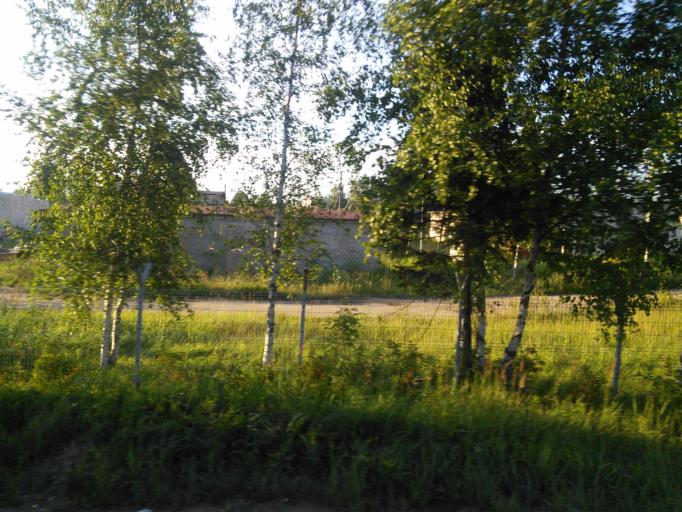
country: RU
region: Vologda
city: Chagoda
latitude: 59.1602
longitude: 35.3262
